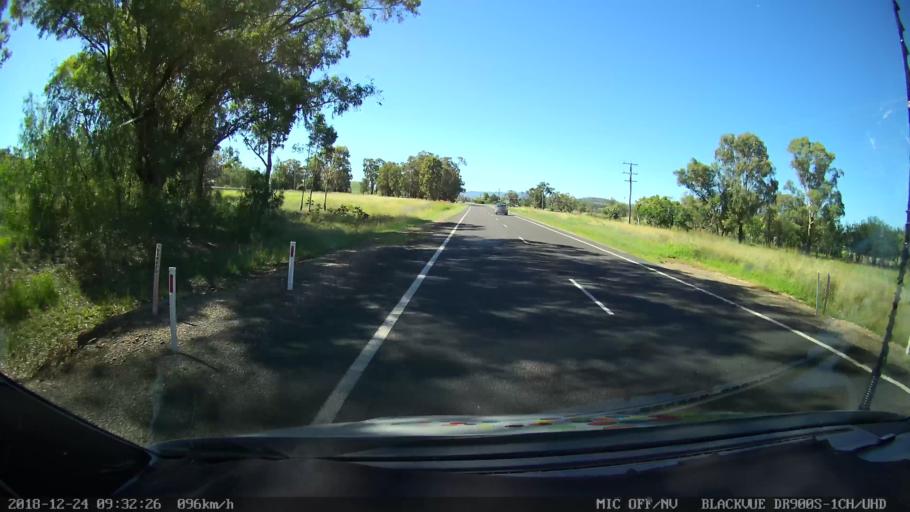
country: AU
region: New South Wales
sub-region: Liverpool Plains
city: Quirindi
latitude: -31.5903
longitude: 150.7024
